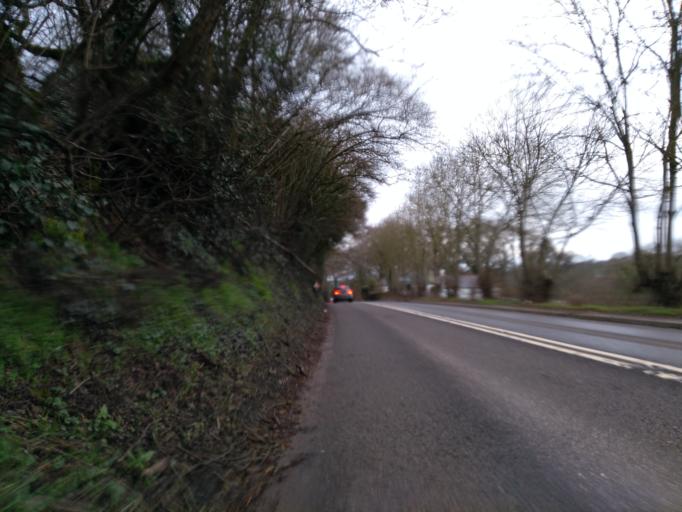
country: GB
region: England
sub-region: Devon
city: Exeter
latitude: 50.7574
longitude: -3.5562
